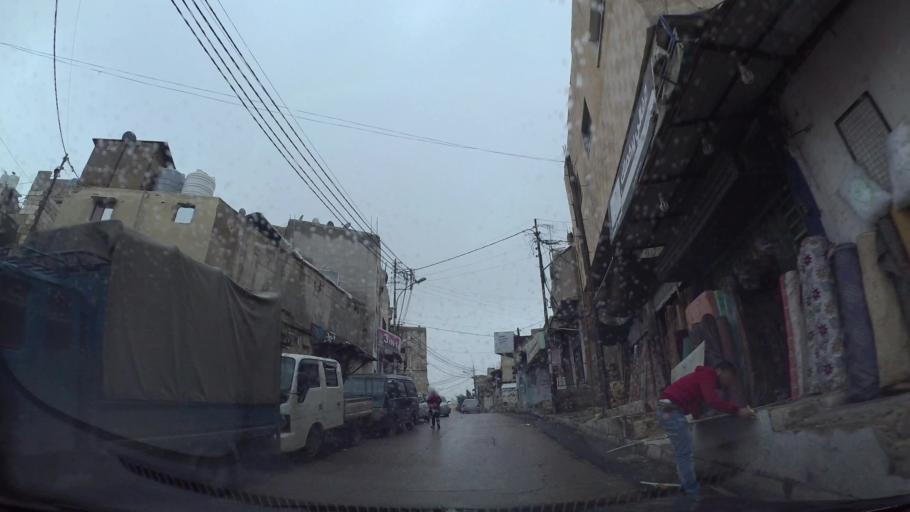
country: JO
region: Amman
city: Amman
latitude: 31.9697
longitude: 35.9258
